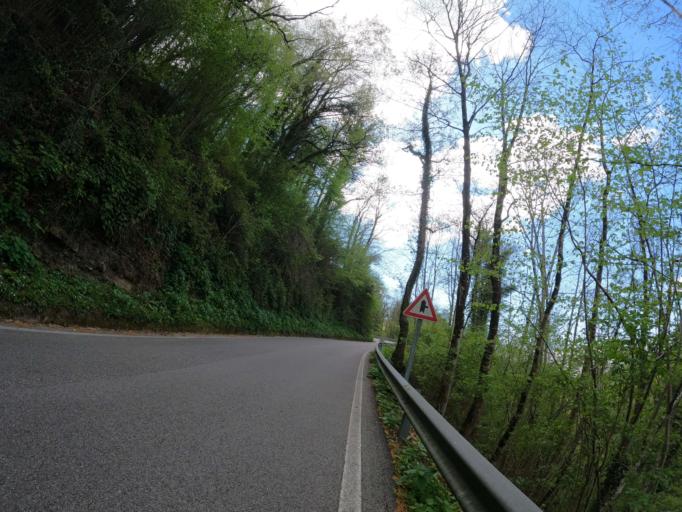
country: IT
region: Friuli Venezia Giulia
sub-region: Provincia di Udine
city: Stregna
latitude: 46.1283
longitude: 13.5717
